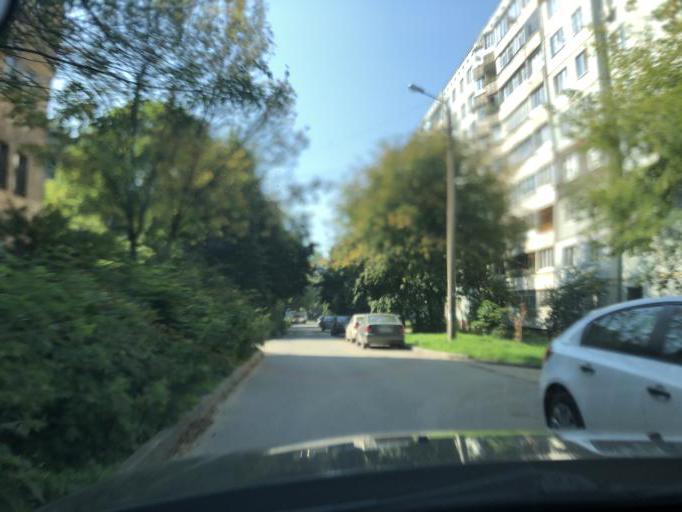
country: RU
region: Tula
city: Tula
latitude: 54.2097
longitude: 37.6069
